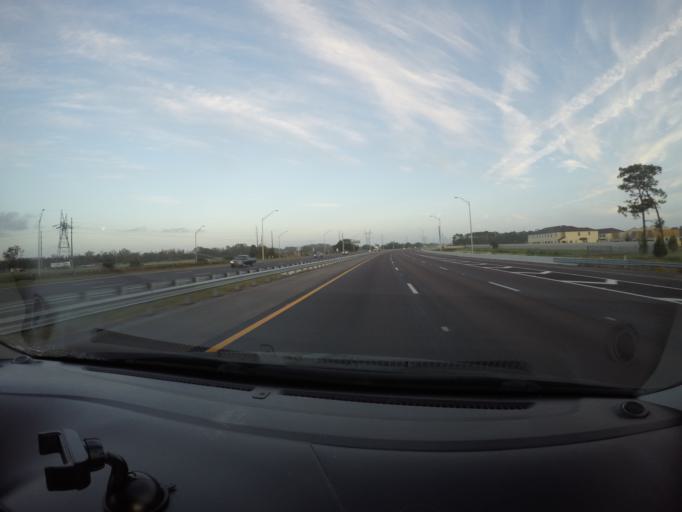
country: US
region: Florida
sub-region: Orange County
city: Azalea Park
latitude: 28.5133
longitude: -81.2493
